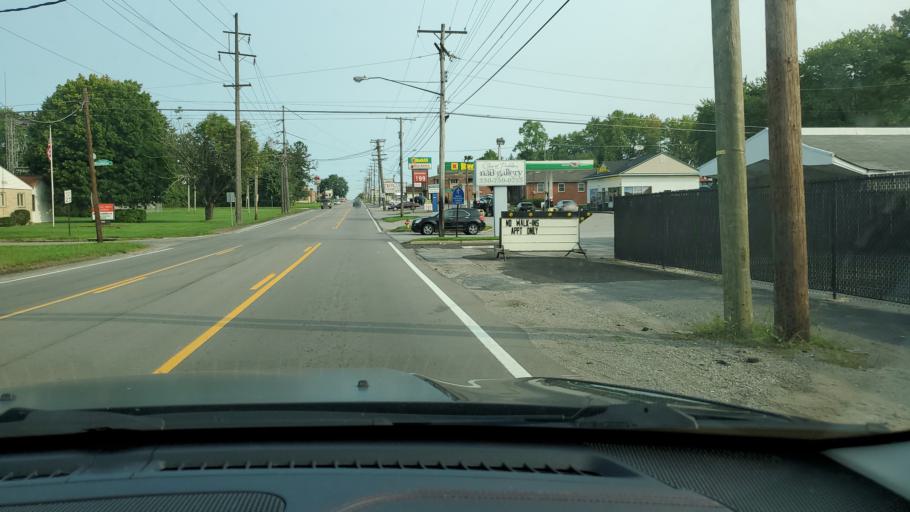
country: US
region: Ohio
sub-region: Mahoning County
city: Struthers
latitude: 41.0535
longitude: -80.6158
